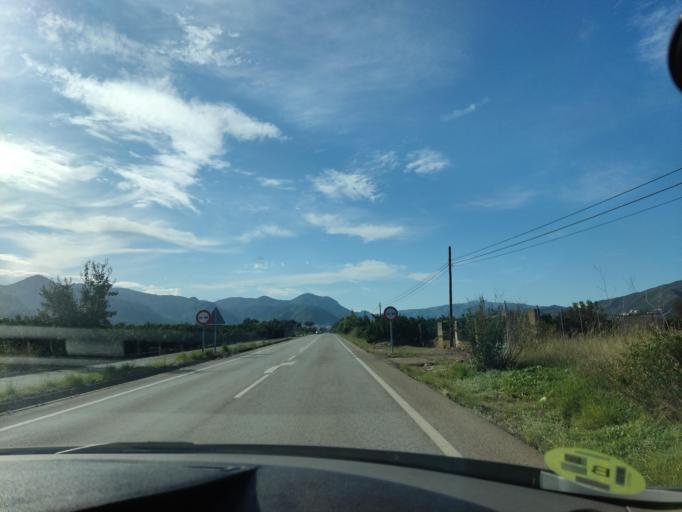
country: ES
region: Valencia
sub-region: Provincia de Alicante
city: Pego
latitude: 38.8472
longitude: -0.0854
